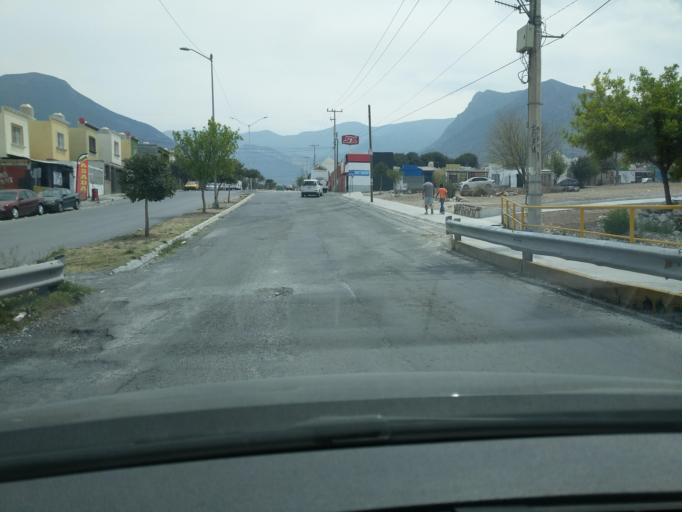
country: MX
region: Coahuila
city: Saltillo
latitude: 25.3536
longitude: -101.0150
